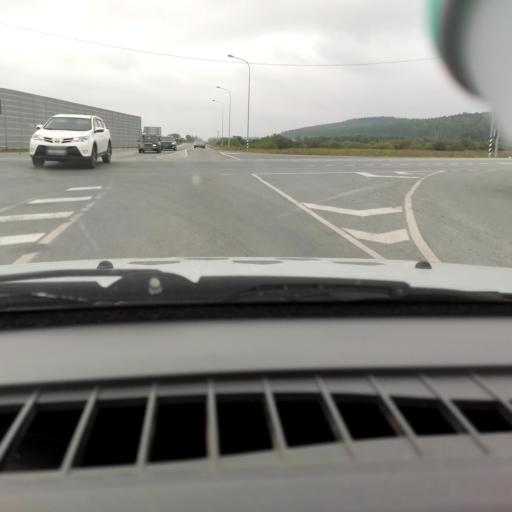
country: RU
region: Chelyabinsk
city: Miass
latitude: 54.9439
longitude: 60.0508
